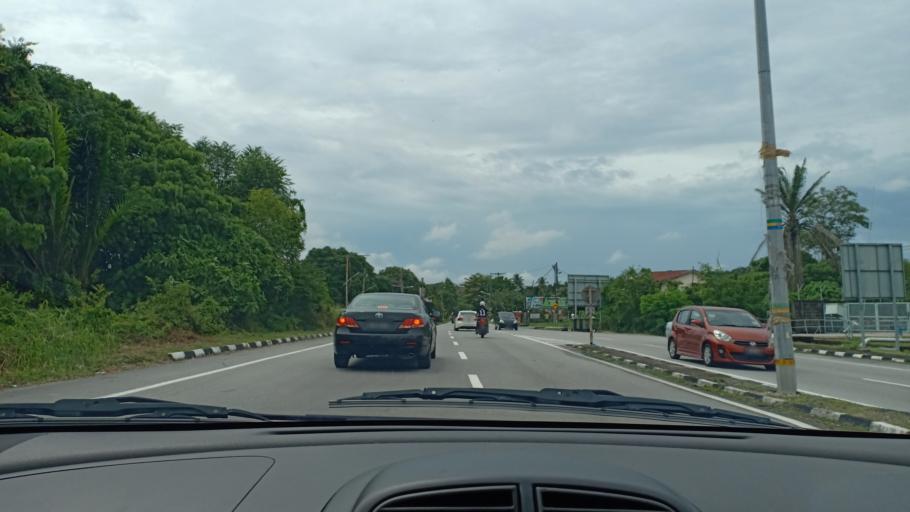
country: MY
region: Penang
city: Bukit Mertajam
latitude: 5.4072
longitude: 100.4855
